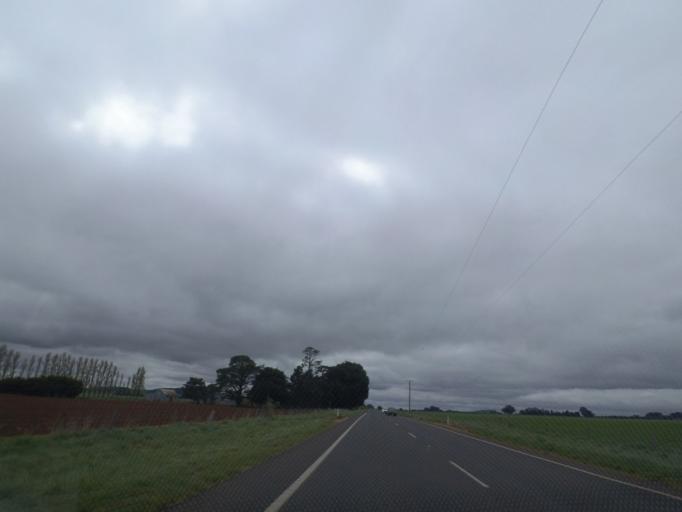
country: AU
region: Victoria
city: Brown Hill
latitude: -37.3939
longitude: 143.9992
